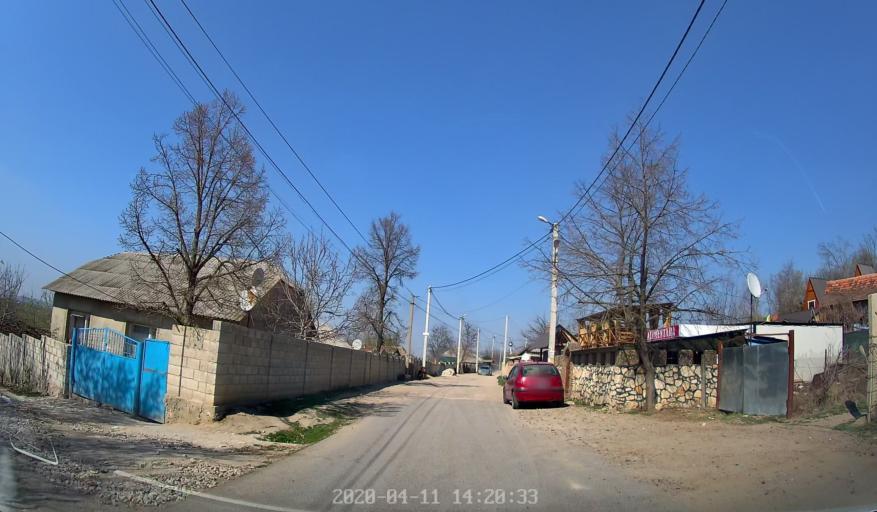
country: MD
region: Chisinau
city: Vadul lui Voda
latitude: 47.0858
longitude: 29.1342
